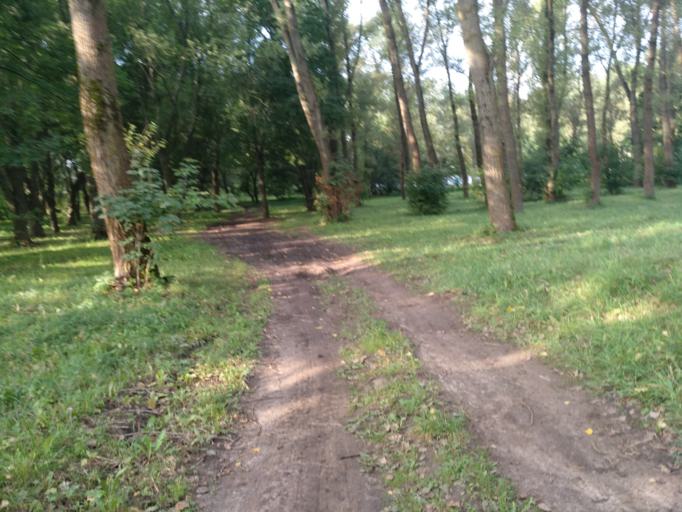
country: BY
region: Minsk
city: Minsk
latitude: 53.9423
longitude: 27.5640
